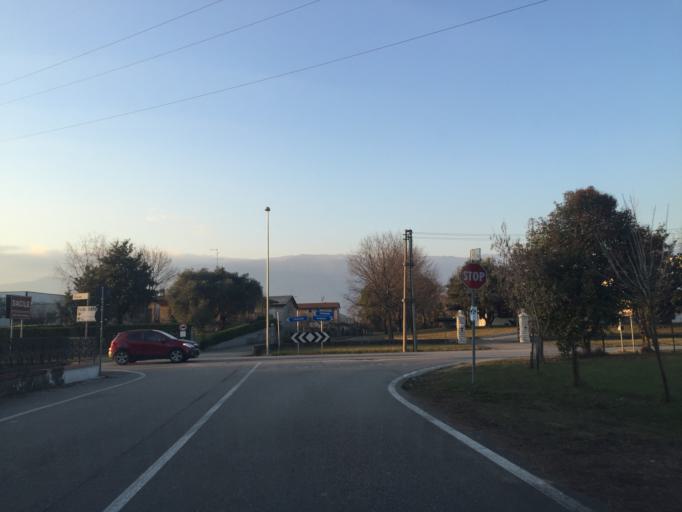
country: IT
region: Friuli Venezia Giulia
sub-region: Provincia di Pordenone
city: Sacile
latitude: 45.9725
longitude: 12.5241
